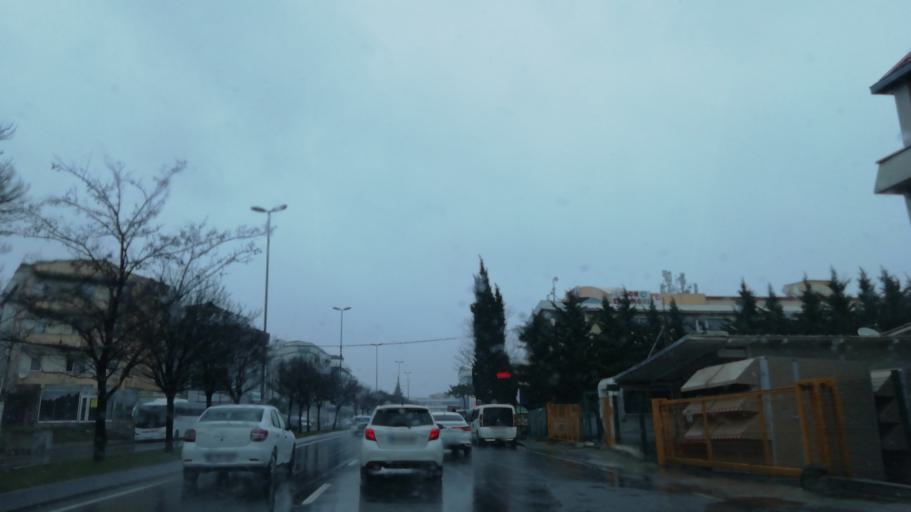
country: TR
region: Istanbul
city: Yakuplu
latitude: 40.9979
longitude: 28.7137
